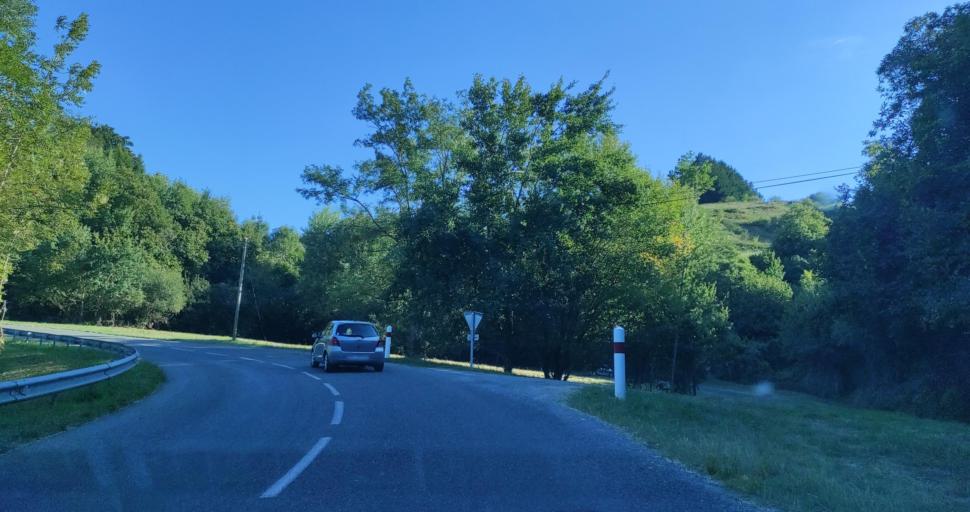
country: FR
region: Midi-Pyrenees
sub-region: Departement de l'Aveyron
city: Firmi
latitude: 44.5191
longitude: 2.3052
